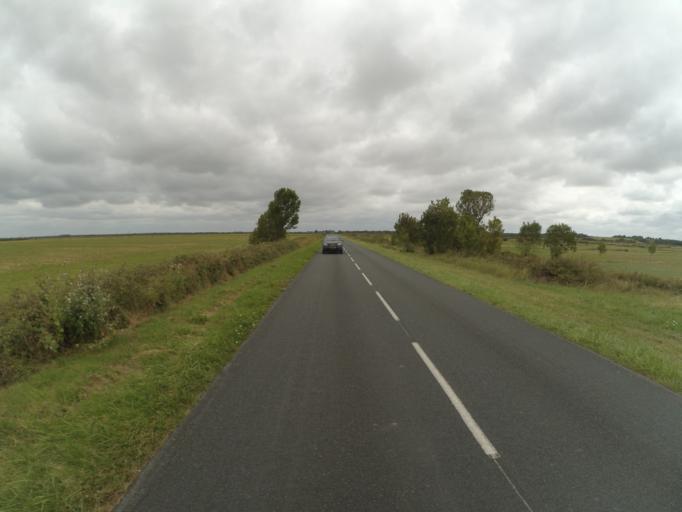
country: FR
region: Pays de la Loire
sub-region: Departement de la Vendee
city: Triaize
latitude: 46.4058
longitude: -1.2964
